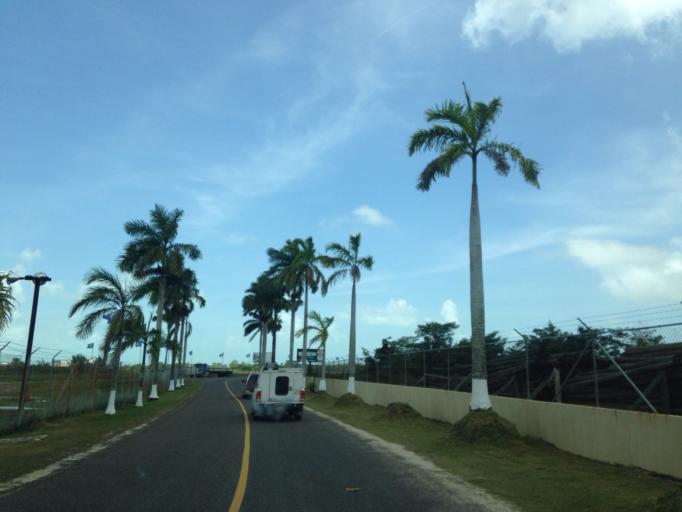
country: BZ
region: Belize
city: Belize City
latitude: 17.5367
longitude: -88.3059
